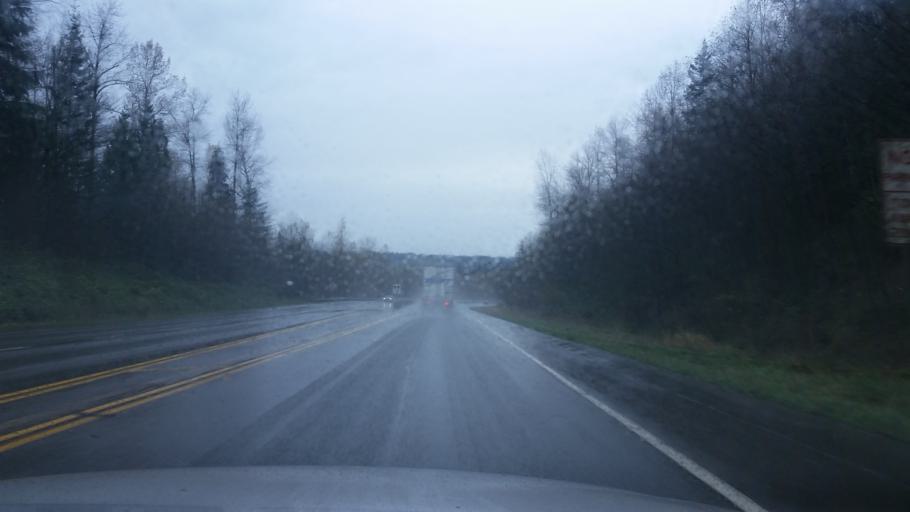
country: US
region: Washington
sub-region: King County
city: Hobart
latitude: 47.4393
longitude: -121.9638
